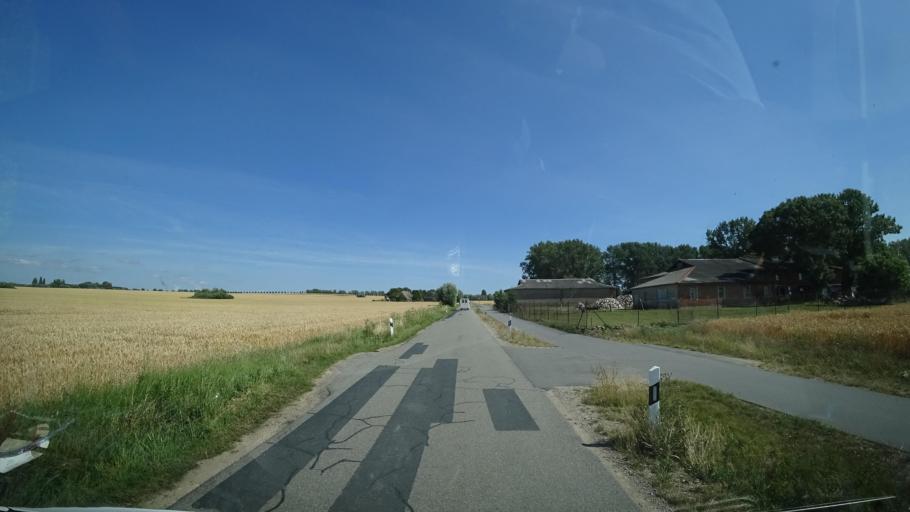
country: DE
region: Mecklenburg-Vorpommern
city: Blowatz
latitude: 54.0236
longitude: 11.5507
